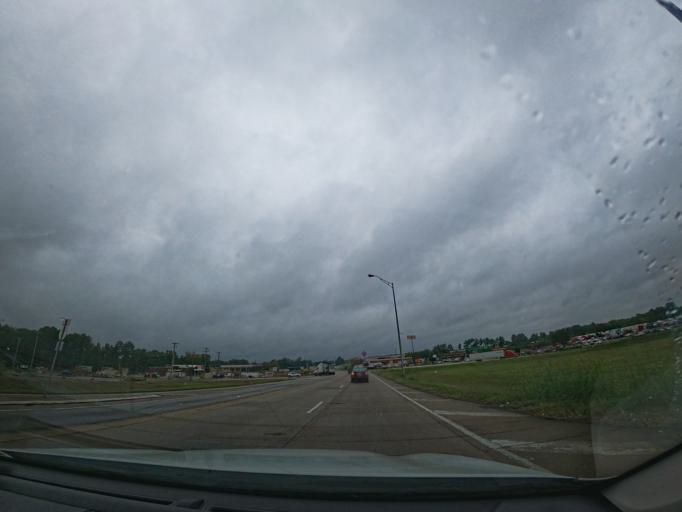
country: US
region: Louisiana
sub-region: Caddo Parish
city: Greenwood
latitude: 32.4463
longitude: -93.8996
